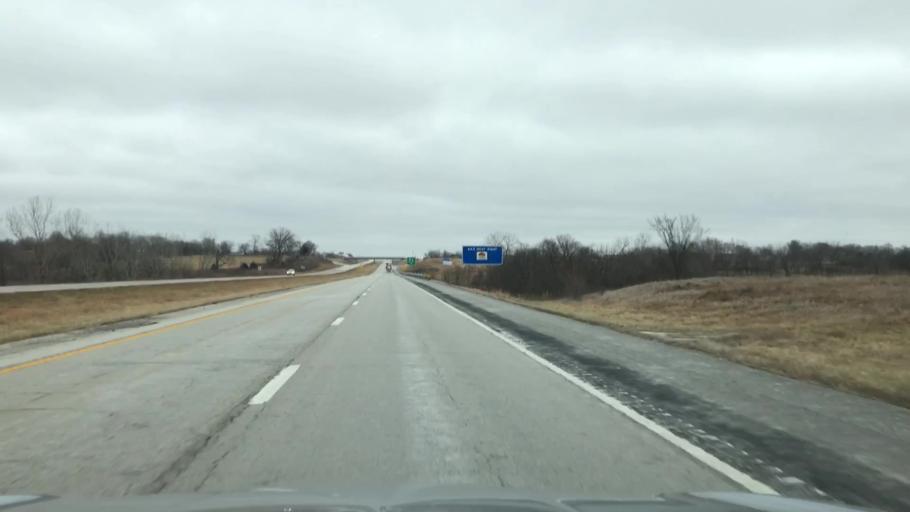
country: US
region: Missouri
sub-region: Caldwell County
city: Hamilton
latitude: 39.7346
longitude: -94.0103
